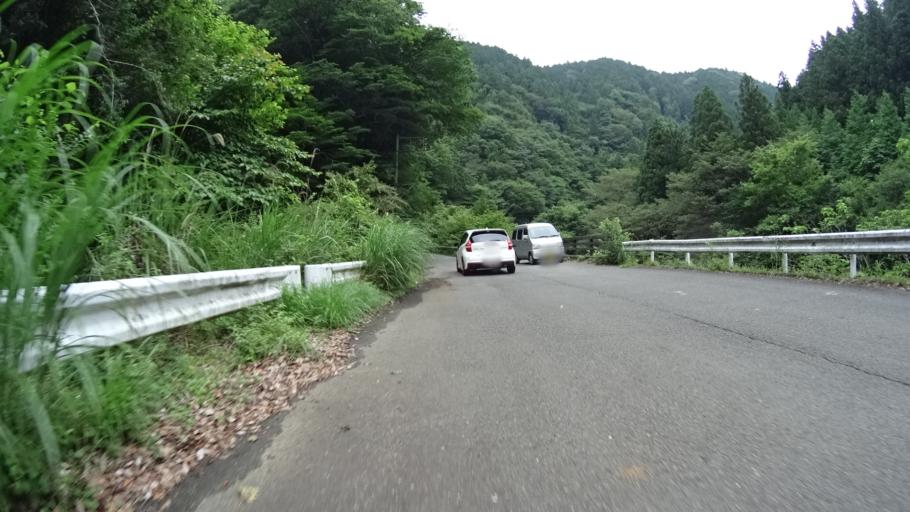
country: JP
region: Kanagawa
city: Hadano
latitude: 35.4645
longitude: 139.2145
